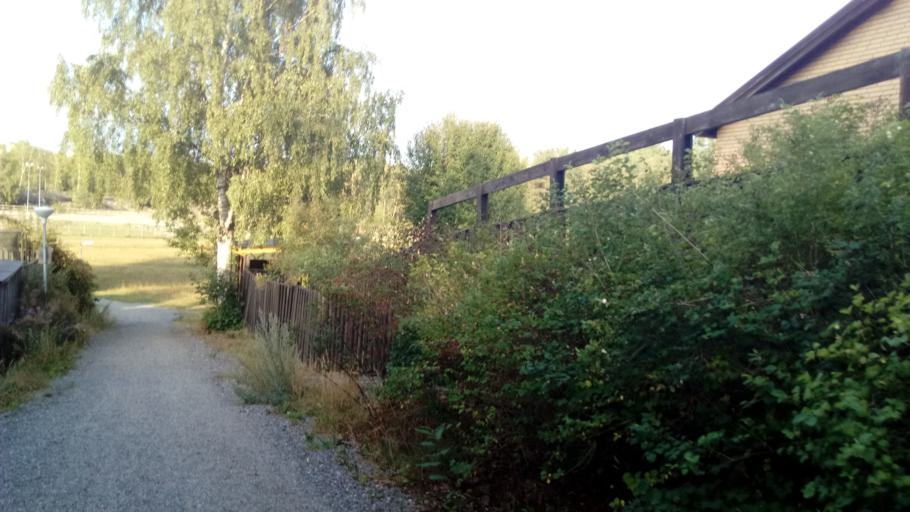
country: SE
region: Stockholm
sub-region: Tyreso Kommun
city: Bollmora
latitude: 59.2423
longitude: 18.2527
